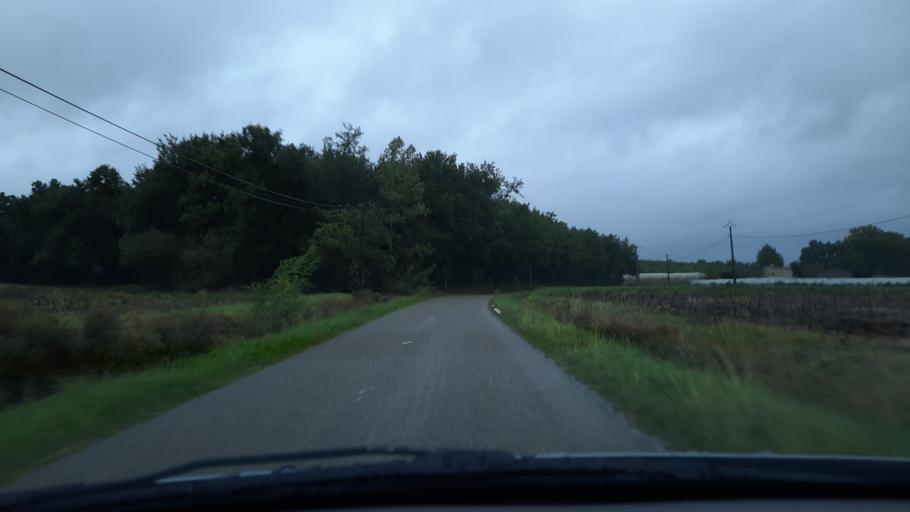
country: FR
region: Midi-Pyrenees
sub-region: Departement du Tarn-et-Garonne
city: Lafrancaise
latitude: 44.1831
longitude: 1.2727
